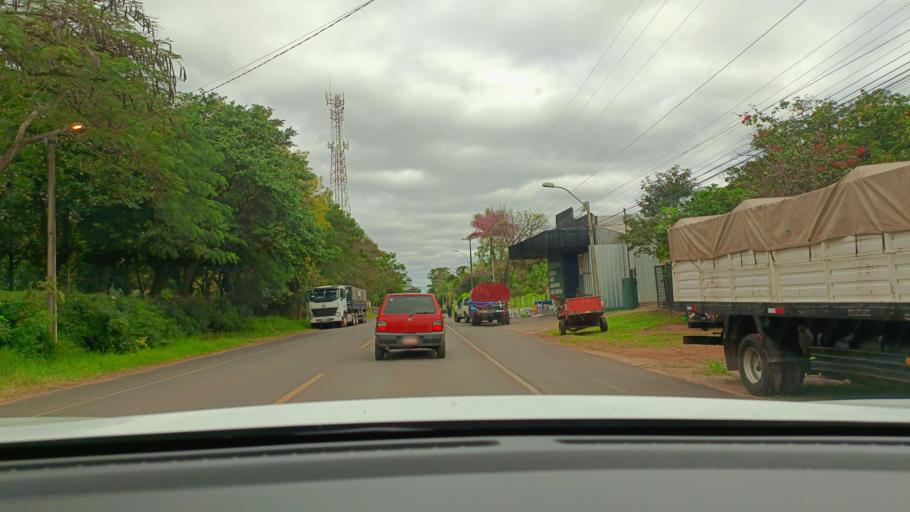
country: PY
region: San Pedro
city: Guayaybi
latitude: -24.6780
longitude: -56.4613
